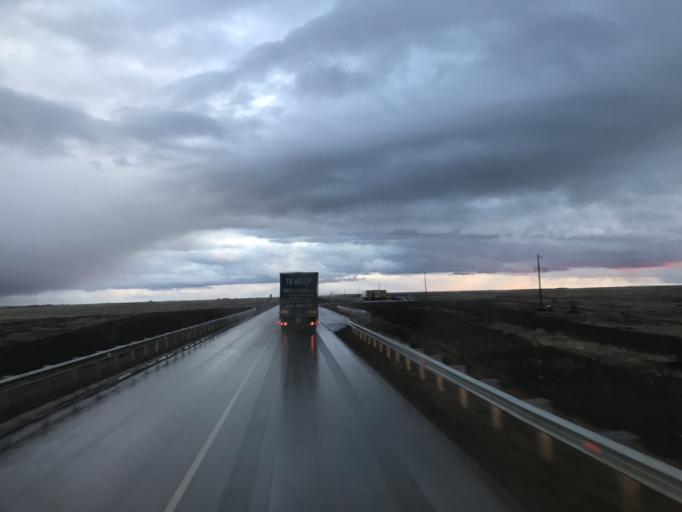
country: KZ
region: Qostanay
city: Ordzhonikidze
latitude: 52.4493
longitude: 61.7716
